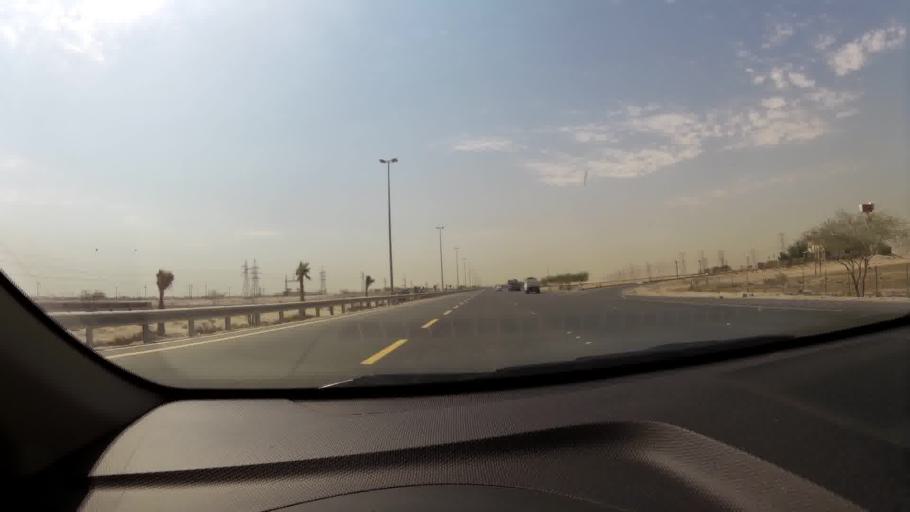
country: KW
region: Al Ahmadi
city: Al Fahahil
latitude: 28.8082
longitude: 48.2661
